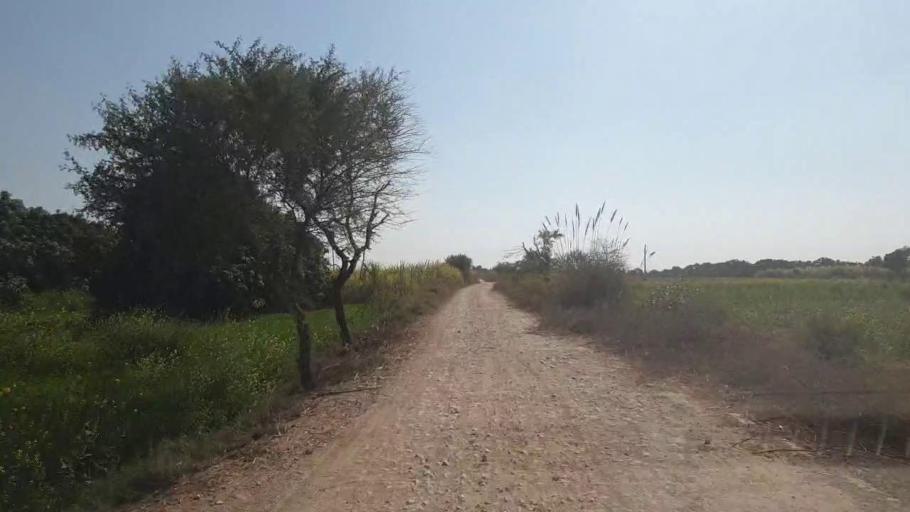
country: PK
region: Sindh
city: Chambar
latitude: 25.3088
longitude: 68.7408
